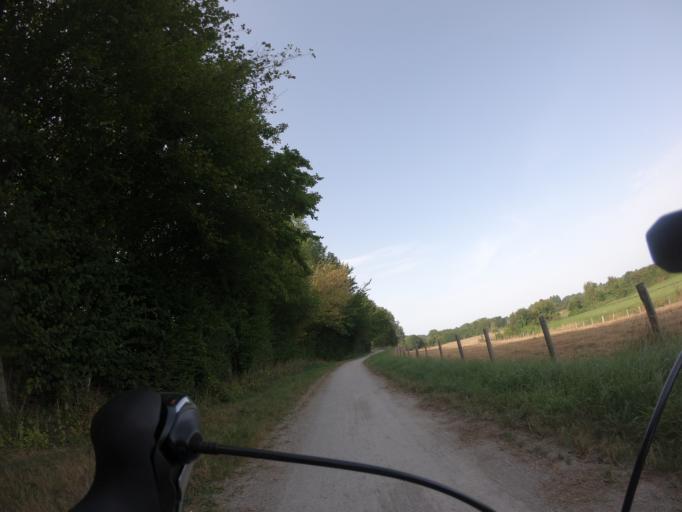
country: FR
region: Lower Normandy
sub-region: Departement de l'Orne
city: Conde-sur-Huisne
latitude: 48.3860
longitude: 0.8513
